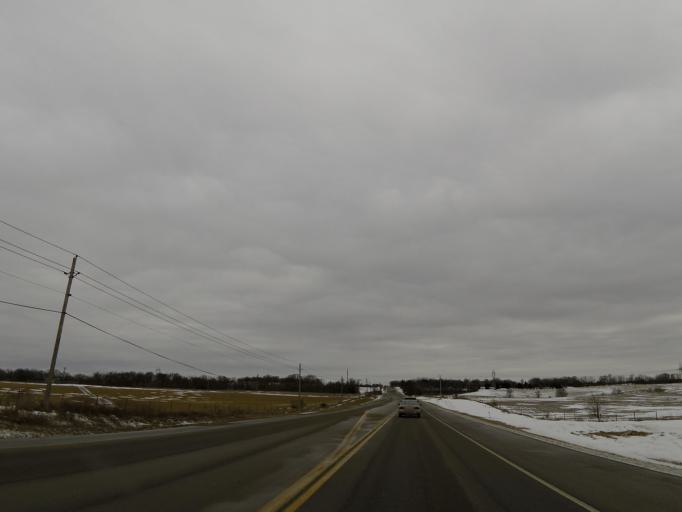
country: US
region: Minnesota
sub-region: Washington County
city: Cottage Grove
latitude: 44.8614
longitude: -92.9031
